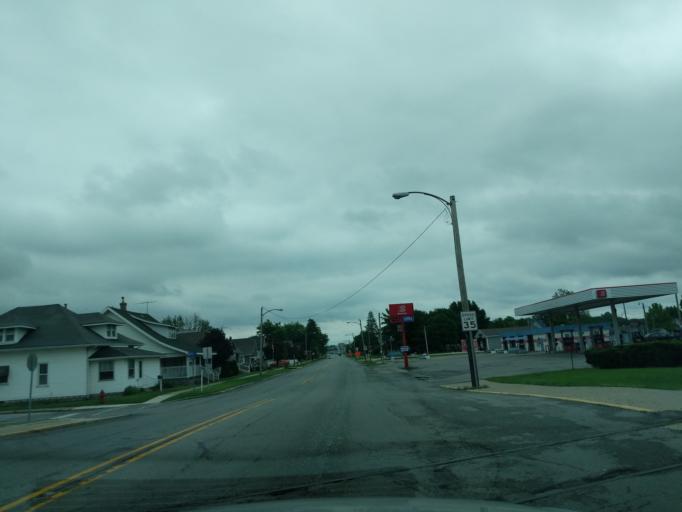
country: US
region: Indiana
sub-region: Tipton County
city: Tipton
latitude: 40.2823
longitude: -86.0371
